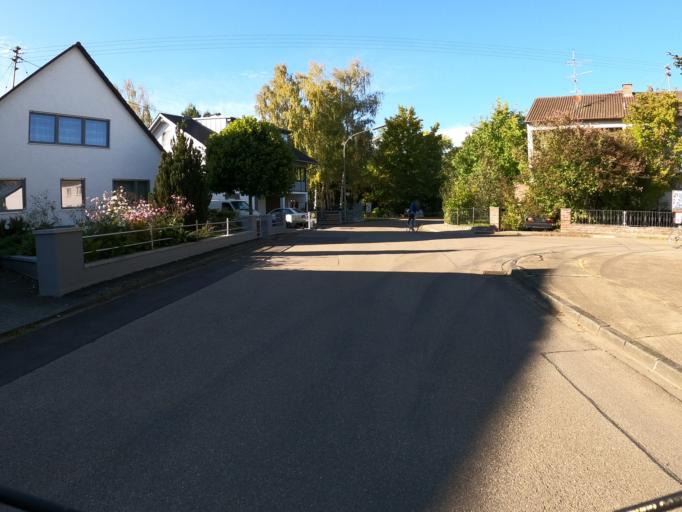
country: DE
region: Bavaria
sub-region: Swabia
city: Nersingen
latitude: 48.4282
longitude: 10.1453
